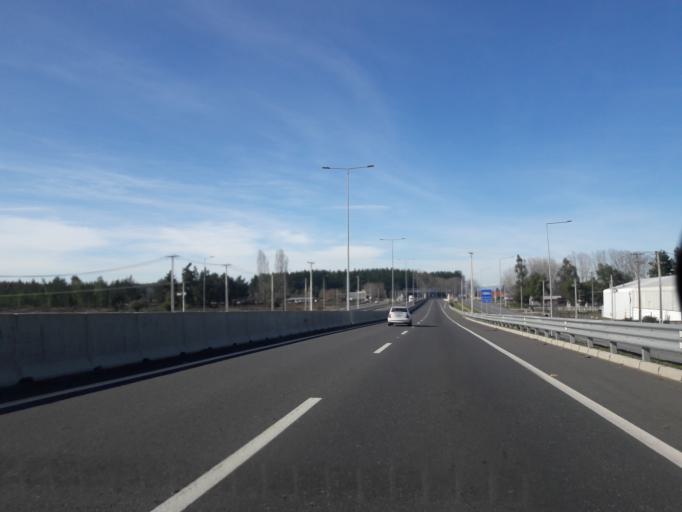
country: CL
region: Biobio
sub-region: Provincia de Biobio
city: Cabrero
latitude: -37.0314
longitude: -72.4274
